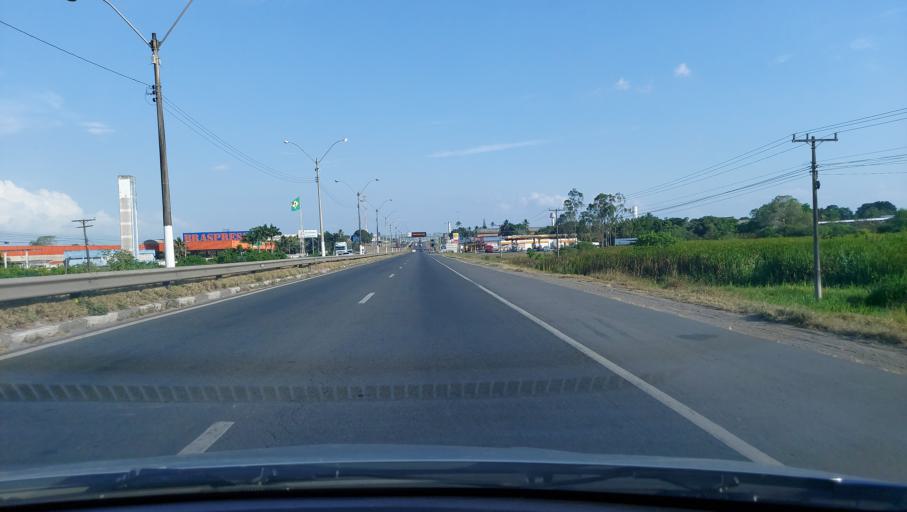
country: BR
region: Bahia
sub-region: Feira De Santana
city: Feira de Santana
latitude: -12.2768
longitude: -38.9296
